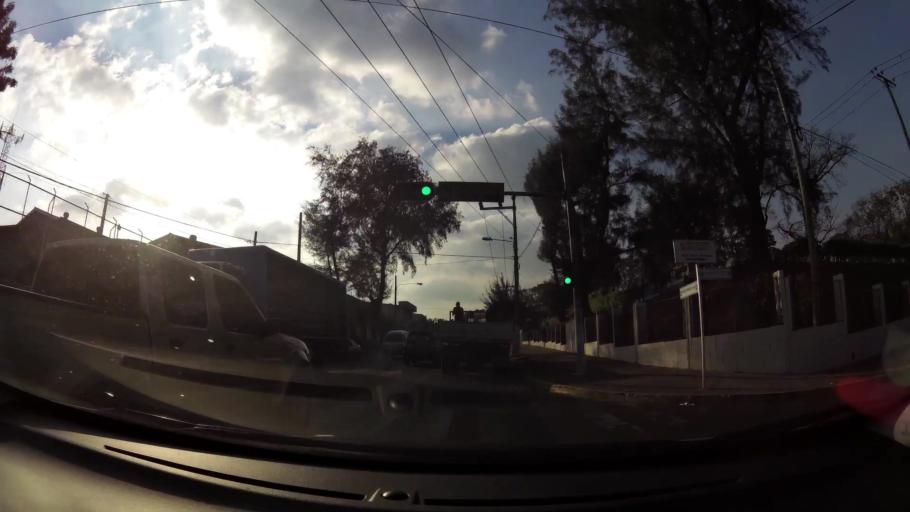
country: SV
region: San Salvador
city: San Salvador
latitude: 13.6924
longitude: -89.2007
